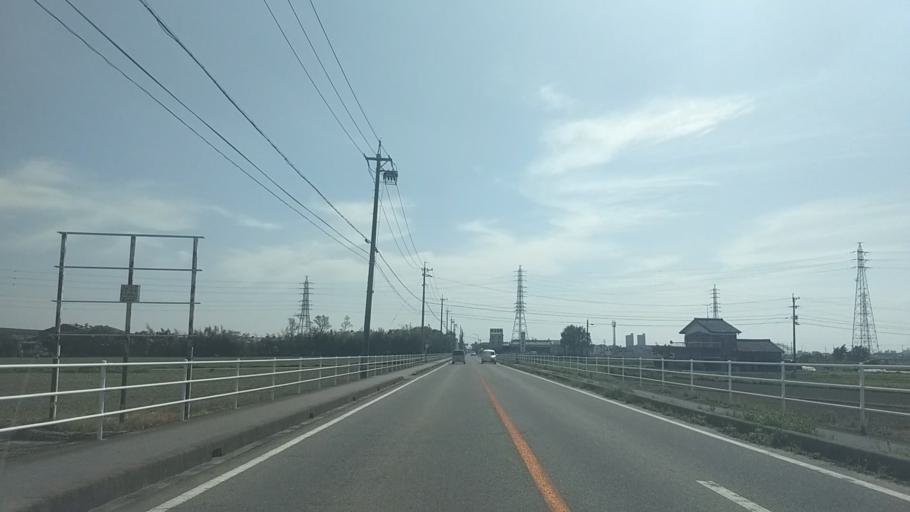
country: JP
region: Aichi
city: Anjo
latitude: 34.9748
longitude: 137.1112
